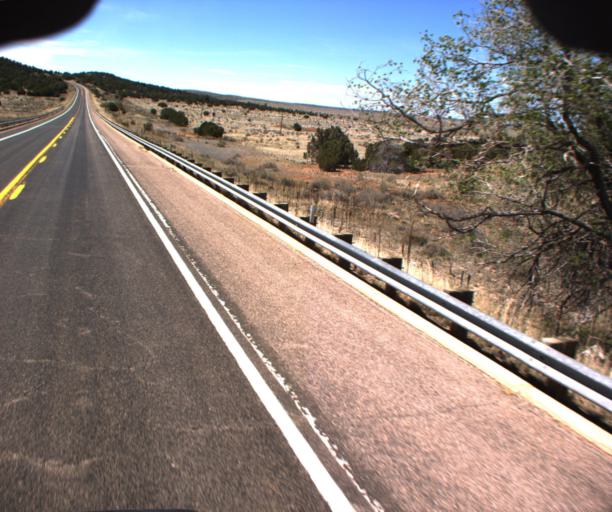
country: US
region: Arizona
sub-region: Mohave County
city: Peach Springs
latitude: 35.5212
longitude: -113.2070
